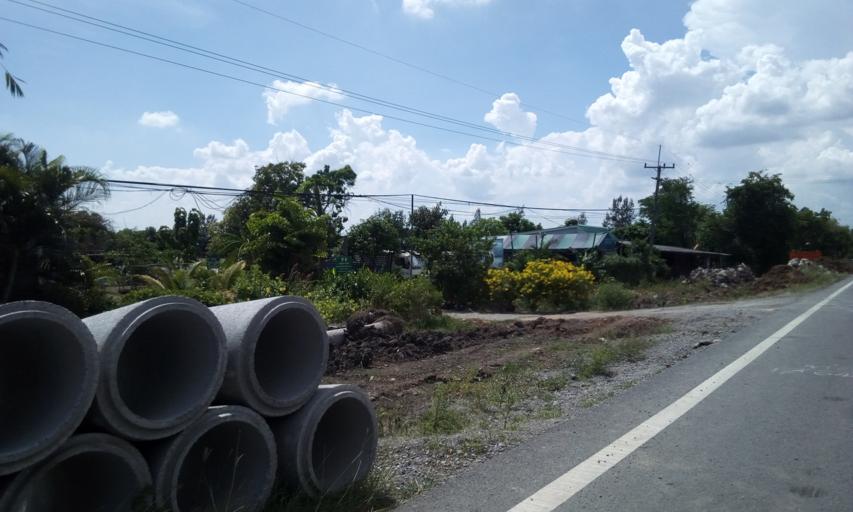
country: TH
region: Nakhon Nayok
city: Ongkharak
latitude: 14.0895
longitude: 100.9143
